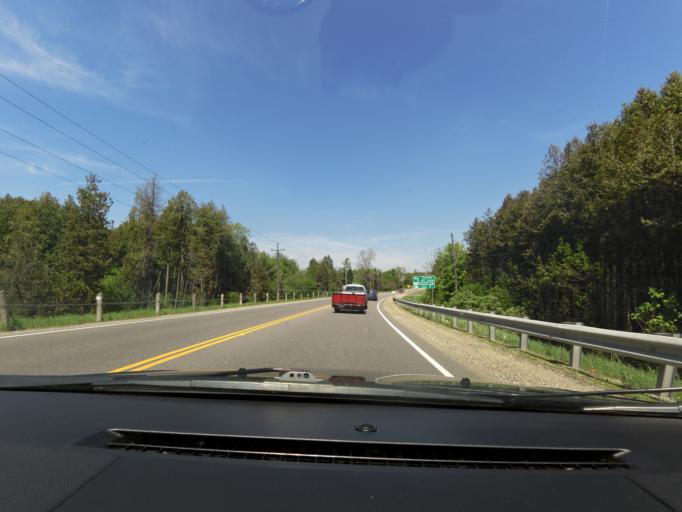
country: CA
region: Ontario
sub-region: Wellington County
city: Guelph
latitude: 43.6066
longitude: -80.1612
